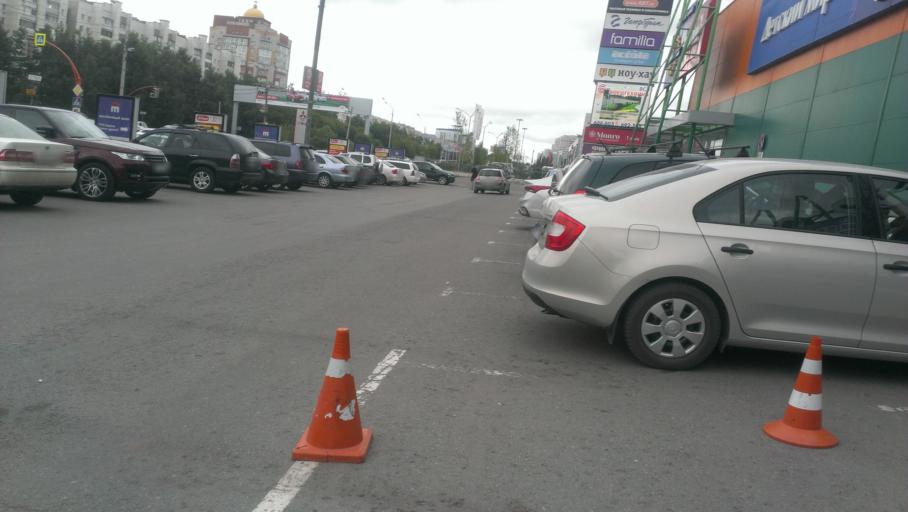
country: RU
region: Altai Krai
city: Novosilikatnyy
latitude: 53.3429
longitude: 83.6827
